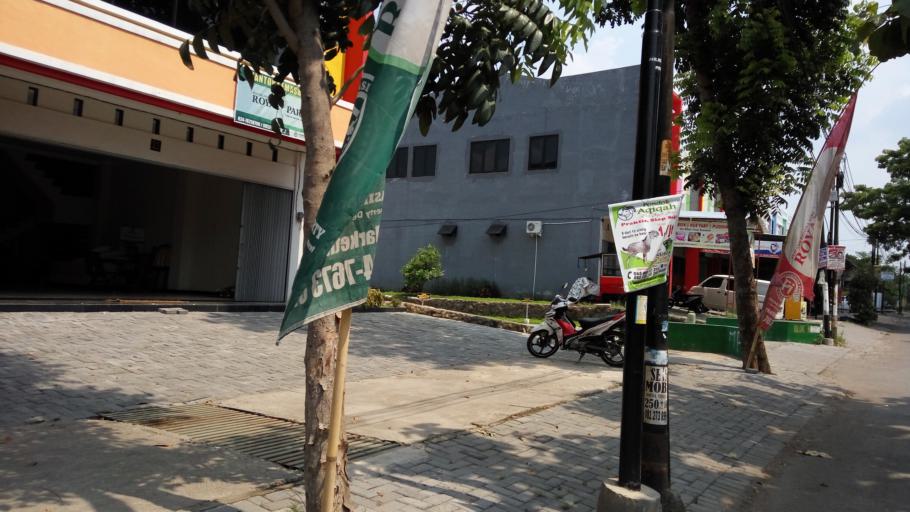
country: ID
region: Central Java
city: Mranggen
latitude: -7.0416
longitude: 110.4794
